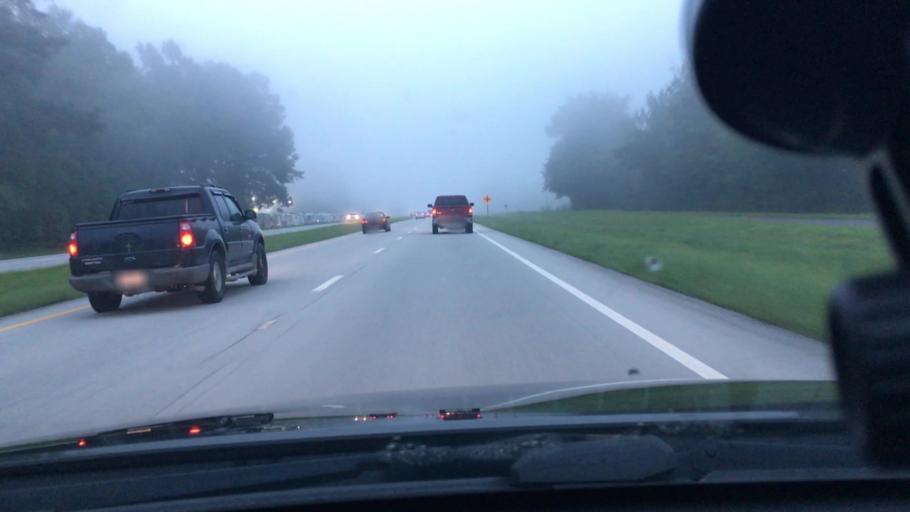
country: US
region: North Carolina
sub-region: Craven County
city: Fairfield Harbour
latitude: 35.0163
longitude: -76.9955
